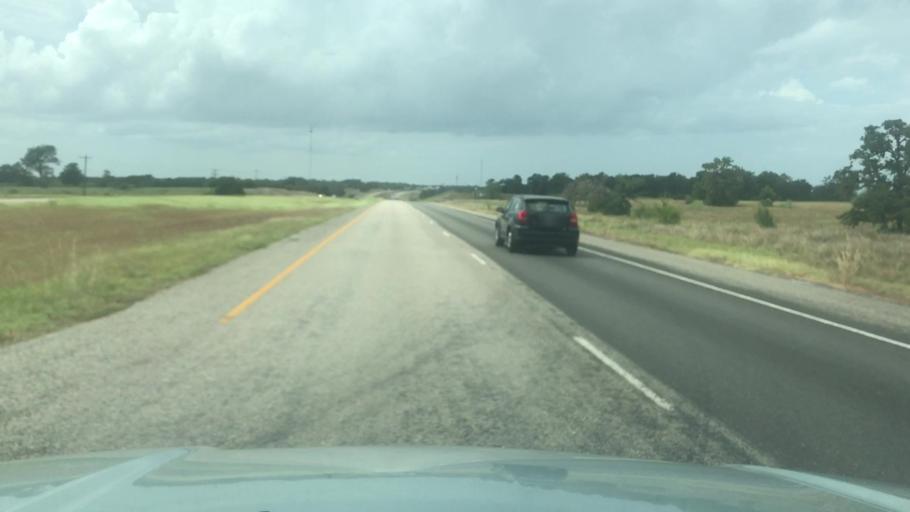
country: US
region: Texas
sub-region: Colorado County
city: Weimar
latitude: 29.7982
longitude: -96.6634
